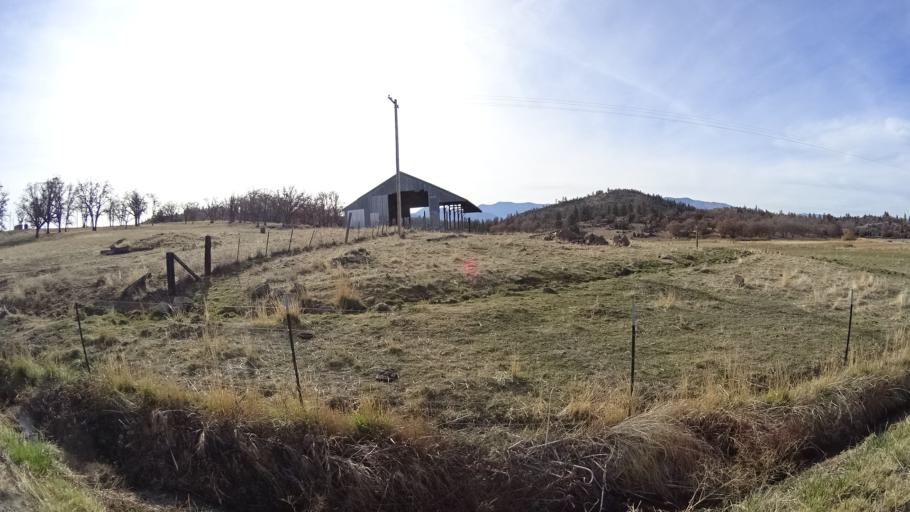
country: US
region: California
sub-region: Siskiyou County
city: Weed
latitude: 41.4570
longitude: -122.3851
